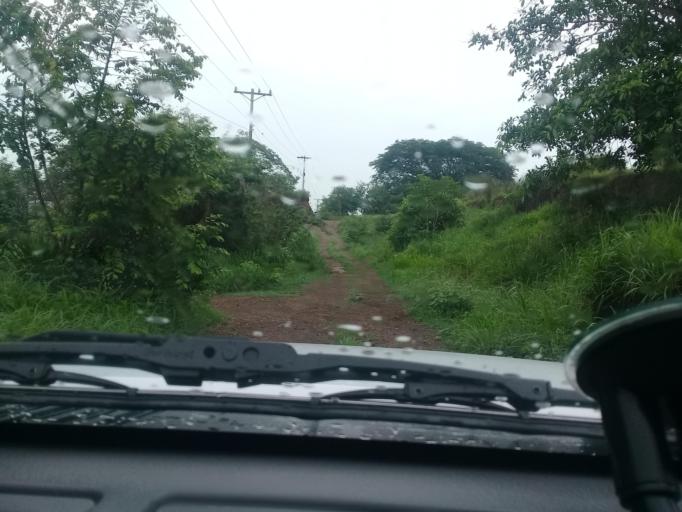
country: MX
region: Veracruz
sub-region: Puente Nacional
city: Cabezas
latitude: 19.3658
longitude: -96.3981
